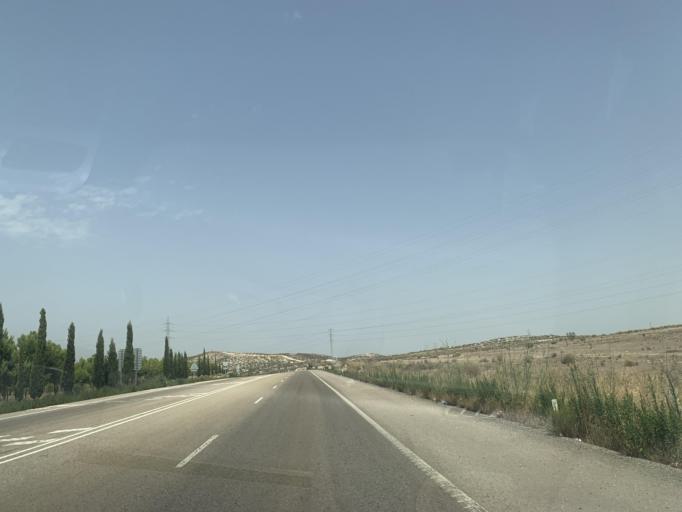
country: ES
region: Aragon
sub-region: Provincia de Zaragoza
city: Zaragoza
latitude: 41.5902
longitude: -0.8313
